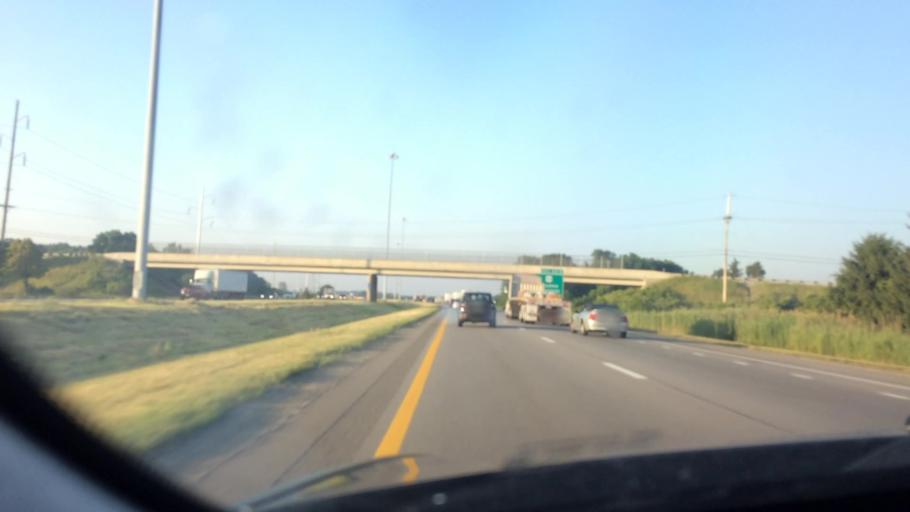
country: US
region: Ohio
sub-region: Lucas County
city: Maumee
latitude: 41.5730
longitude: -83.6914
